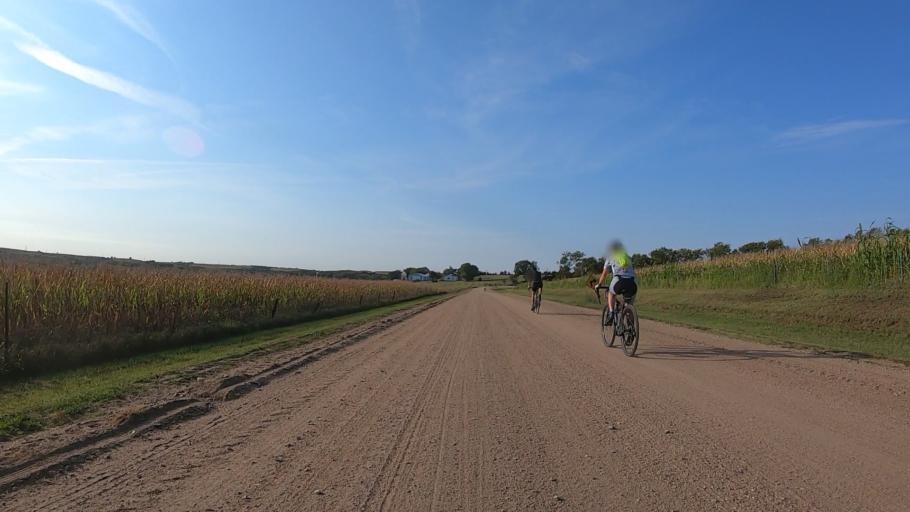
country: US
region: Kansas
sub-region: Marshall County
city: Blue Rapids
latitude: 39.6778
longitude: -96.7839
